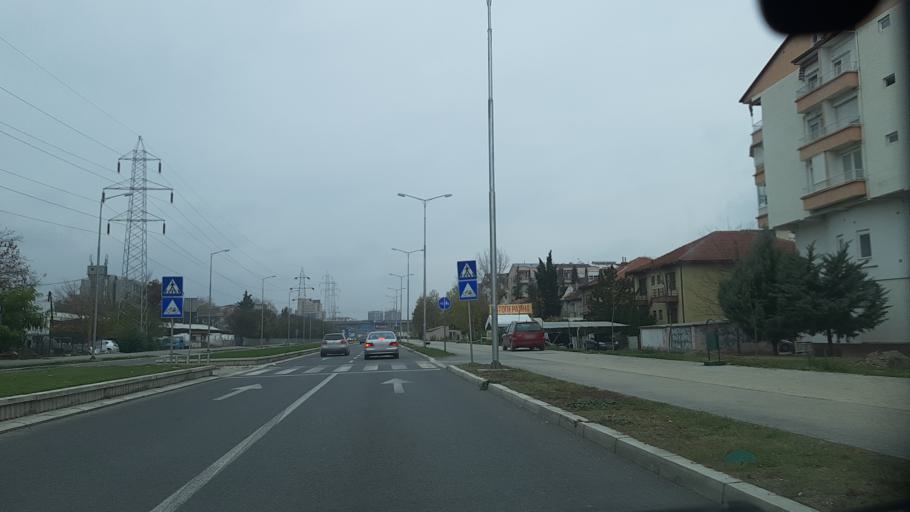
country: MK
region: Karpos
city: Skopje
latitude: 41.9857
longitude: 21.4464
